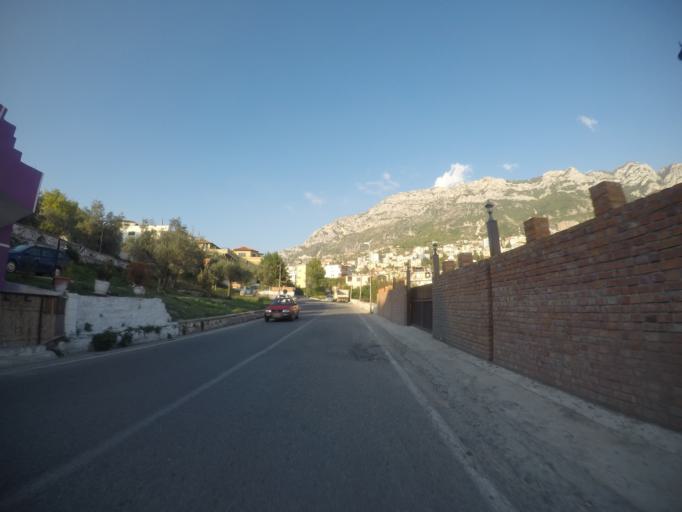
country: AL
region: Durres
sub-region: Rrethi i Krujes
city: Kruje
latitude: 41.5089
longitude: 19.7840
